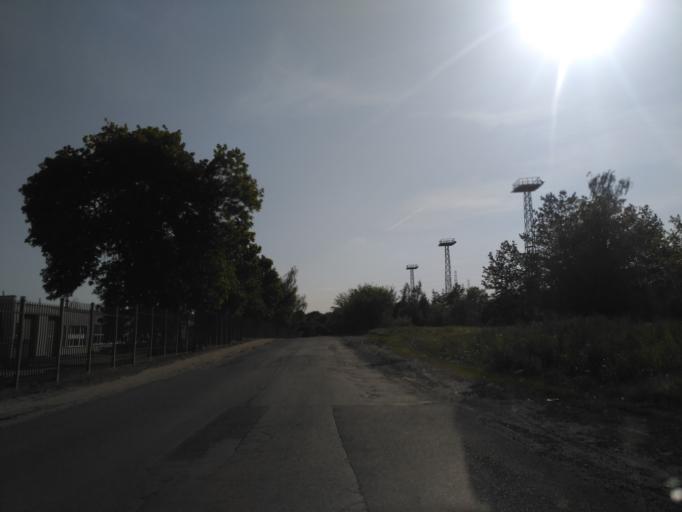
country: PL
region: Lublin Voivodeship
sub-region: Powiat lubelski
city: Lublin
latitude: 51.2143
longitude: 22.5611
